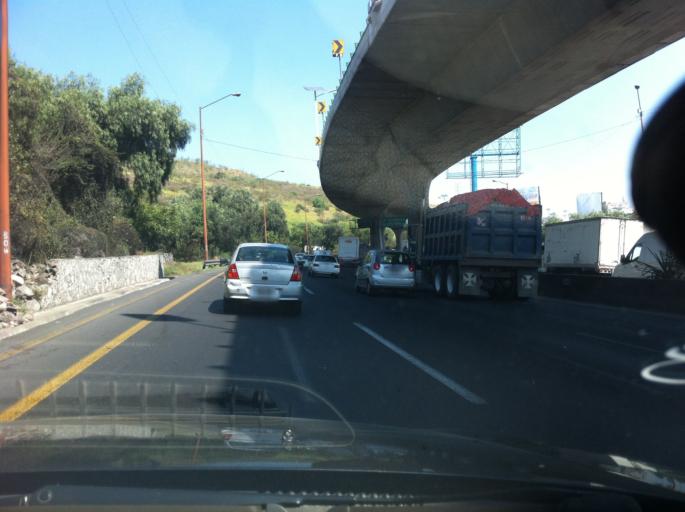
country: MX
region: Mexico
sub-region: Tultitlan
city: Buenavista
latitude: 19.5843
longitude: -99.2045
